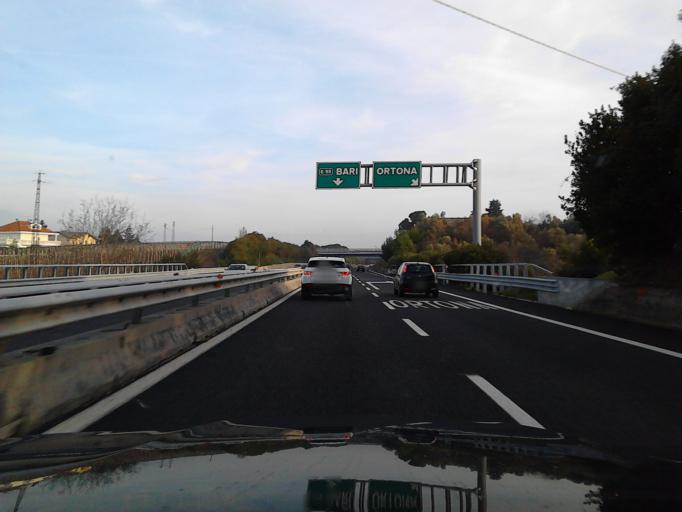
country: IT
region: Abruzzo
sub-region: Provincia di Chieti
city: Ortona
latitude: 42.3322
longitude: 14.3767
